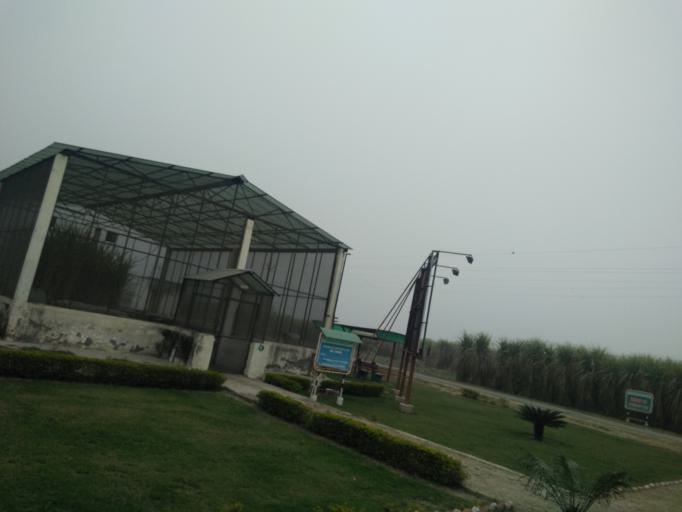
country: IN
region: Uttar Pradesh
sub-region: Lucknow District
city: Lucknow
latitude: 26.8018
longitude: 80.9329
